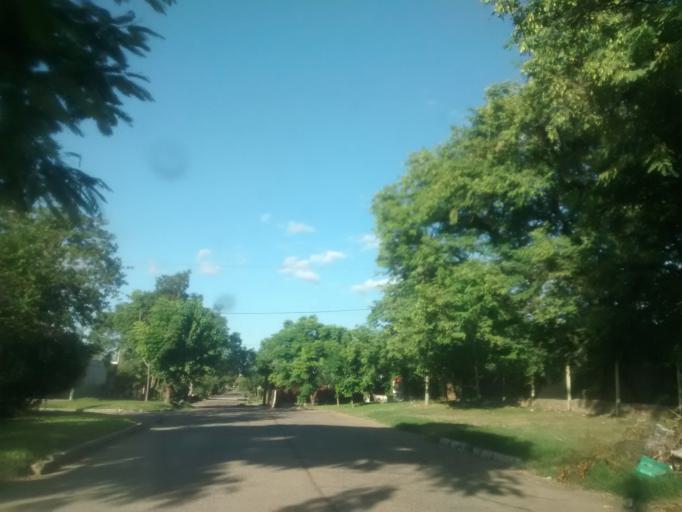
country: AR
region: Chaco
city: Resistencia
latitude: -27.4402
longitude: -58.9771
